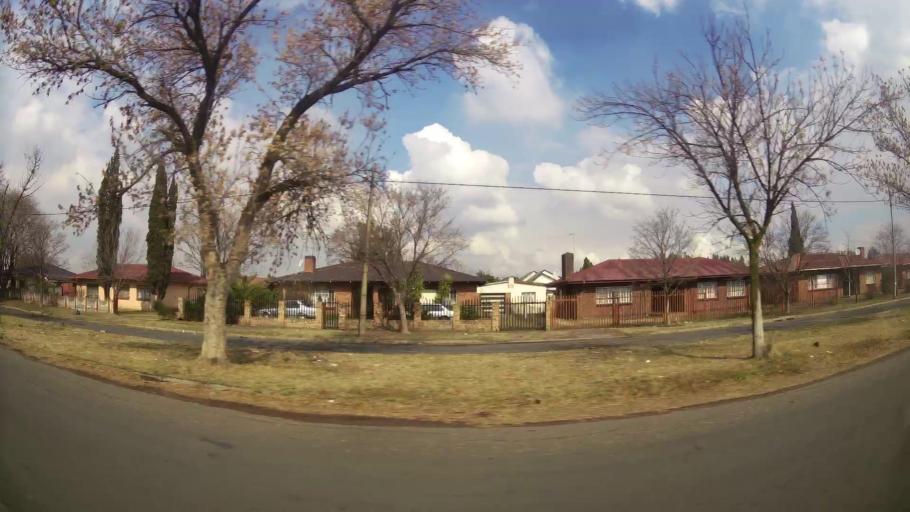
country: ZA
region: Gauteng
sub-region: Sedibeng District Municipality
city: Vereeniging
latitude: -26.6832
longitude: 27.9227
